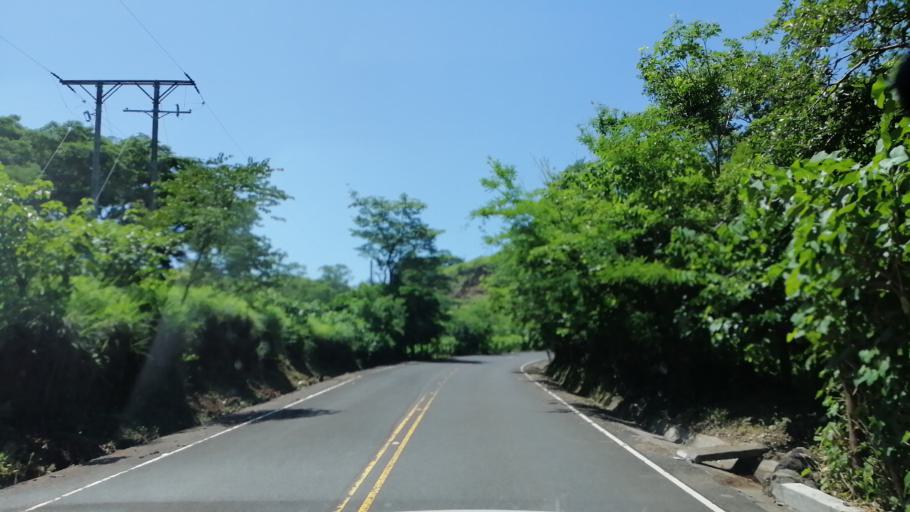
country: SV
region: San Miguel
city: Sesori
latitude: 13.8071
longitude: -88.3902
